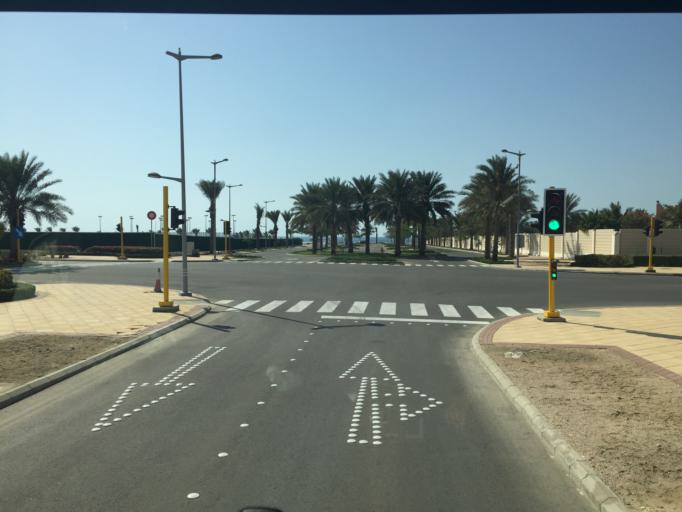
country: SA
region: Makkah
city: Rabigh
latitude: 22.4109
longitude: 39.0789
